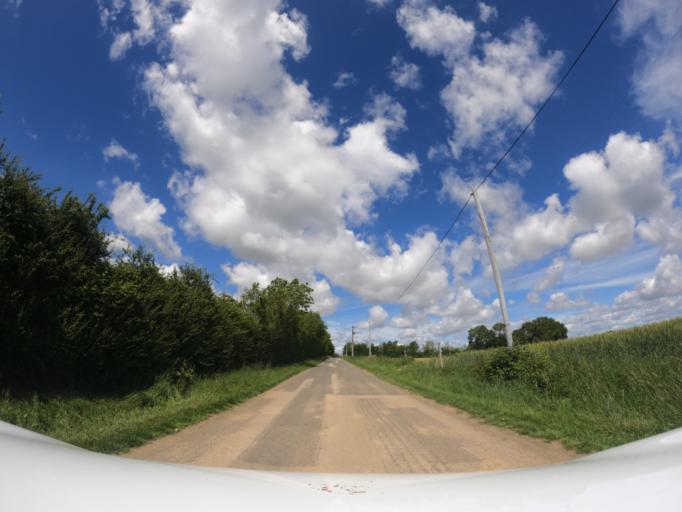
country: FR
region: Pays de la Loire
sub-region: Departement de la Vendee
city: Le Champ-Saint-Pere
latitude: 46.4758
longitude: -1.3206
